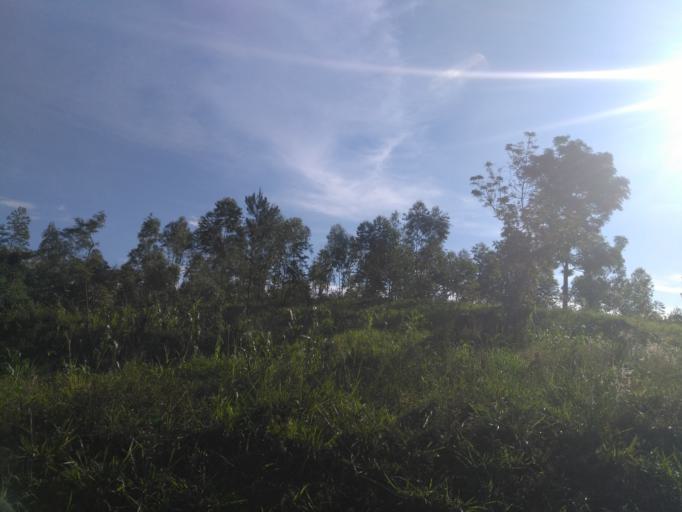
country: UG
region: Eastern Region
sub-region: Jinja District
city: Jinja
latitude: 0.4621
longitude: 33.1826
